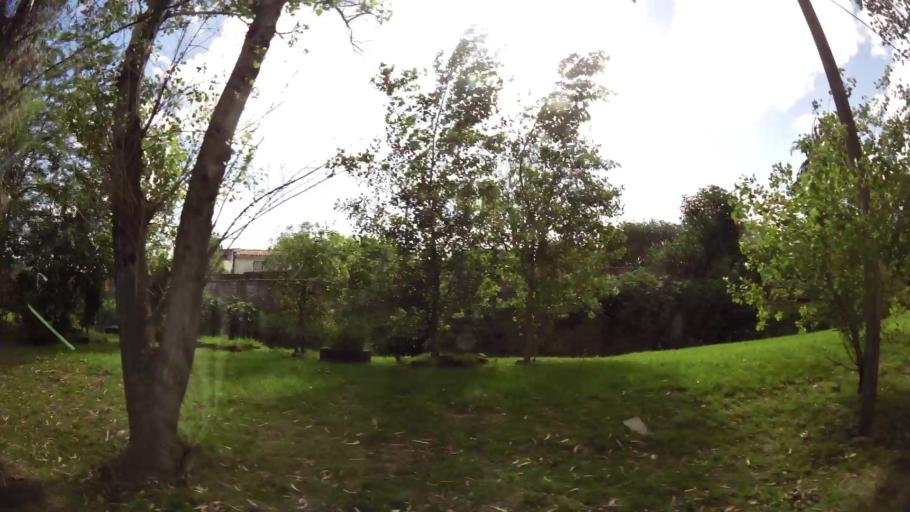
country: UY
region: Canelones
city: La Paz
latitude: -34.8113
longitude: -56.2200
